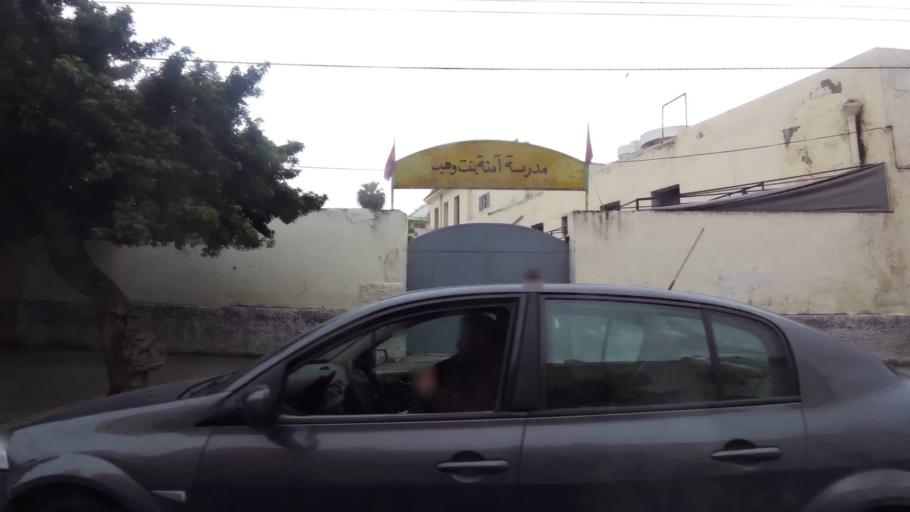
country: MA
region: Grand Casablanca
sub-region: Casablanca
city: Casablanca
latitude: 33.6005
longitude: -7.6324
